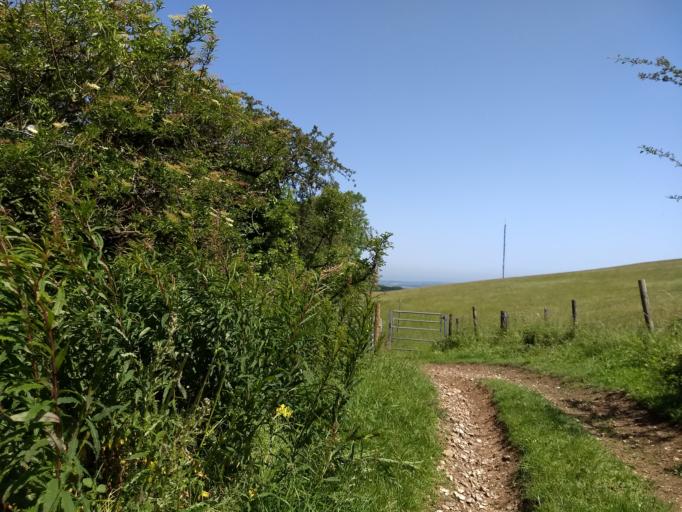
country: GB
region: England
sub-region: Isle of Wight
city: Shalfleet
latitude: 50.6666
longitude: -1.3796
